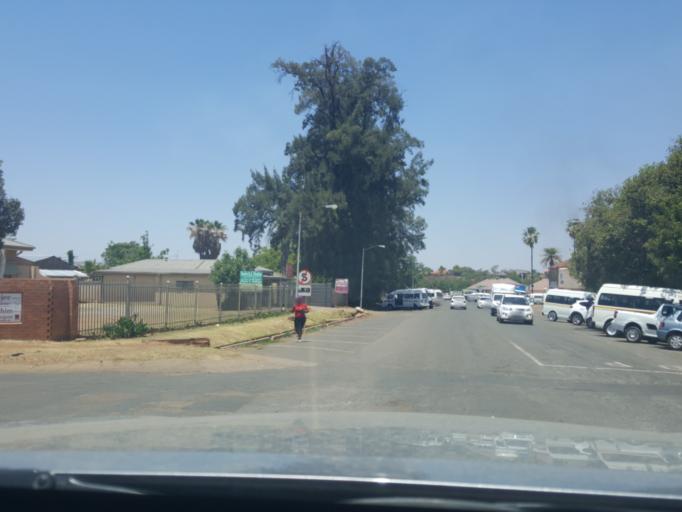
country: ZA
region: North-West
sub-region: Ngaka Modiri Molema District Municipality
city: Zeerust
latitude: -25.5442
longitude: 26.0742
